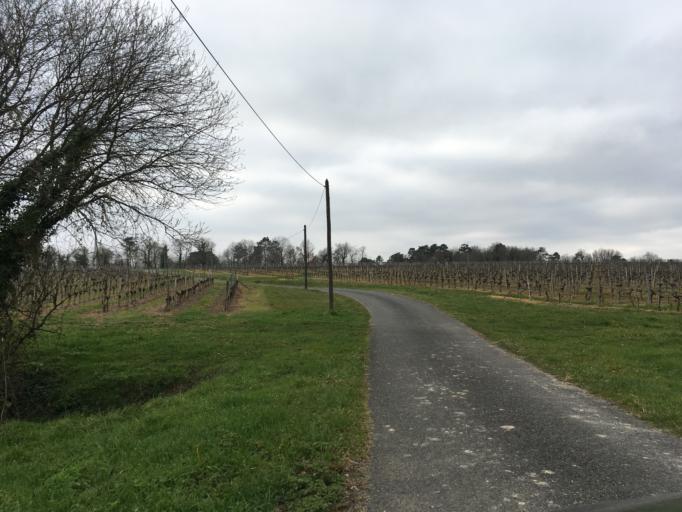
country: FR
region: Aquitaine
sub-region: Departement de la Gironde
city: Saint-Ciers-sur-Gironde
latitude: 45.3101
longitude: -0.6018
